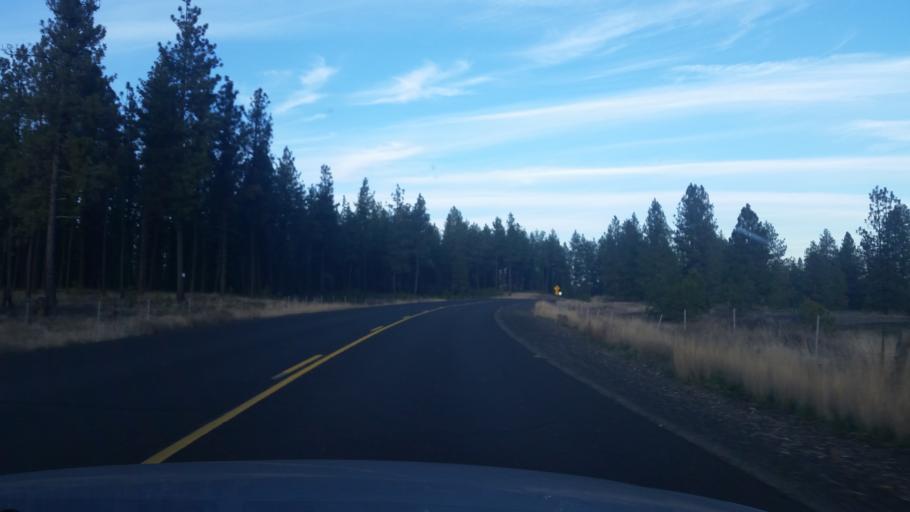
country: US
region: Washington
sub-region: Spokane County
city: Cheney
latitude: 47.4985
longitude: -117.4800
